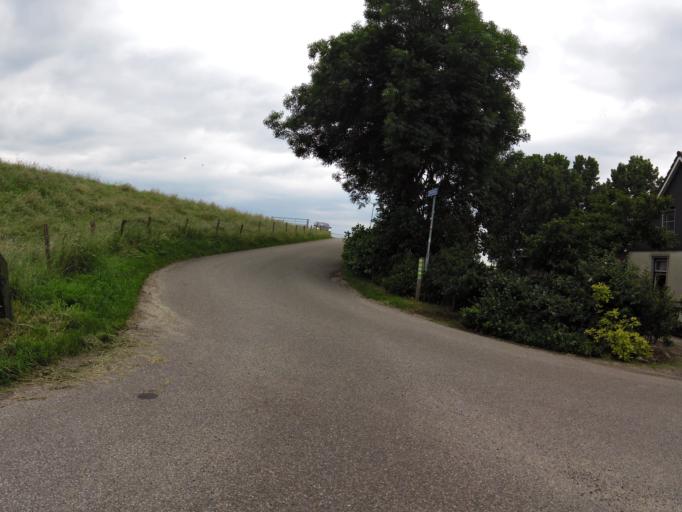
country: NL
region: North Brabant
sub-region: Gemeente Landerd
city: Reek
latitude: 51.7739
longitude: 5.6875
